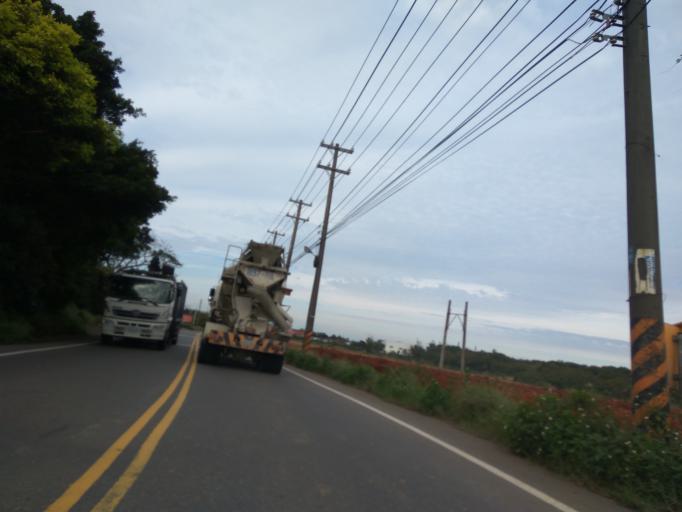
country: TW
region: Taiwan
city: Daxi
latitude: 24.9428
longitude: 121.1543
